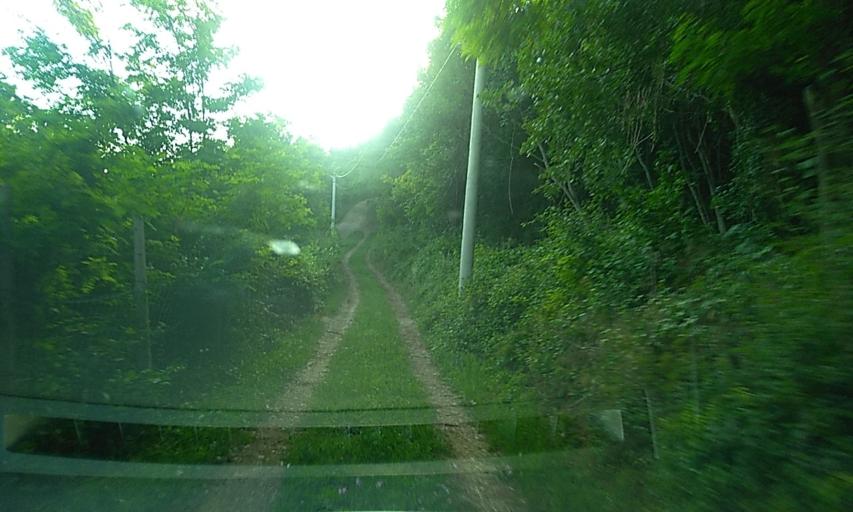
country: RS
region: Central Serbia
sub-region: Nisavski Okrug
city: Niska Banja
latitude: 43.3693
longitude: 21.9958
